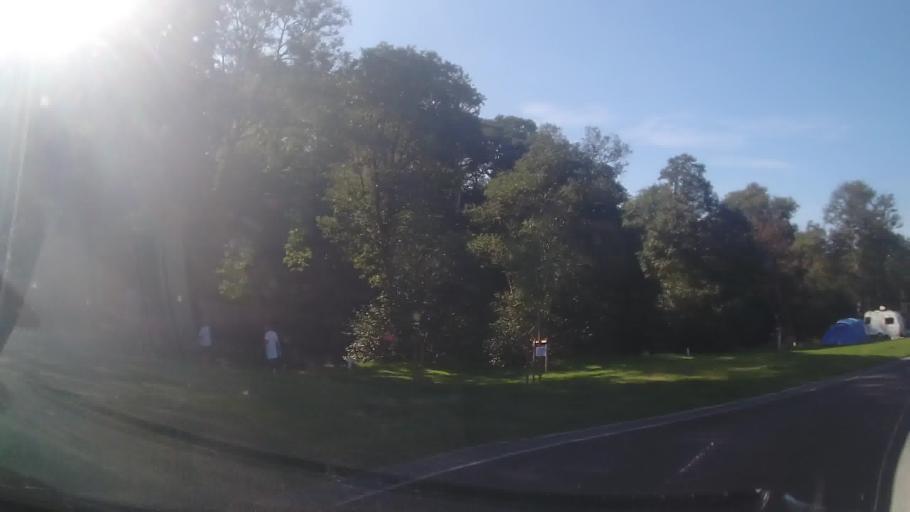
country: GB
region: Wales
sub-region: Sir Powys
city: Rhayader
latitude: 52.3037
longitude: -3.5141
